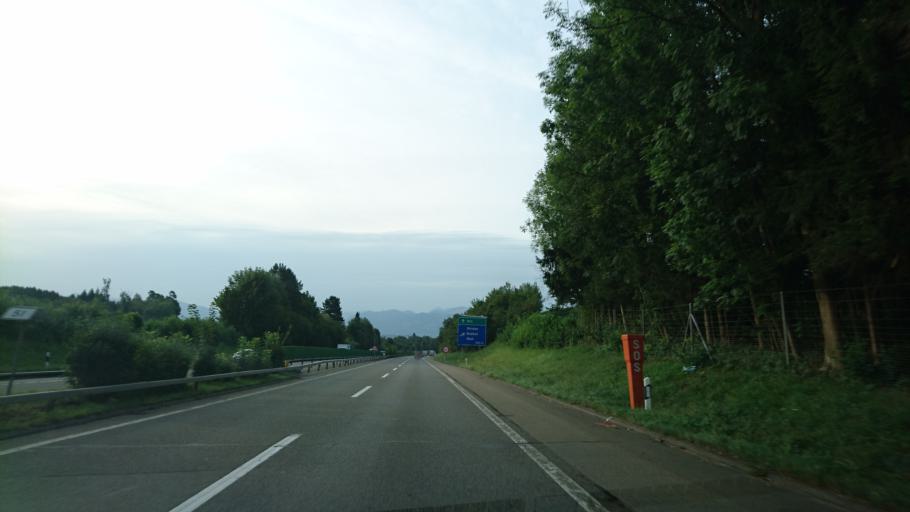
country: CH
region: Zurich
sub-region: Bezirk Hinwil
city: Bubikon
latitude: 47.2798
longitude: 8.8253
